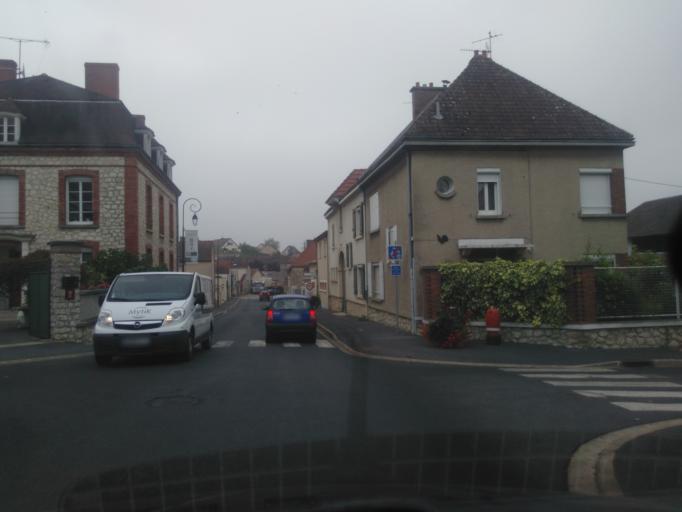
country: FR
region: Champagne-Ardenne
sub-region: Departement de la Marne
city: Mardeuil
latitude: 49.0730
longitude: 3.9289
